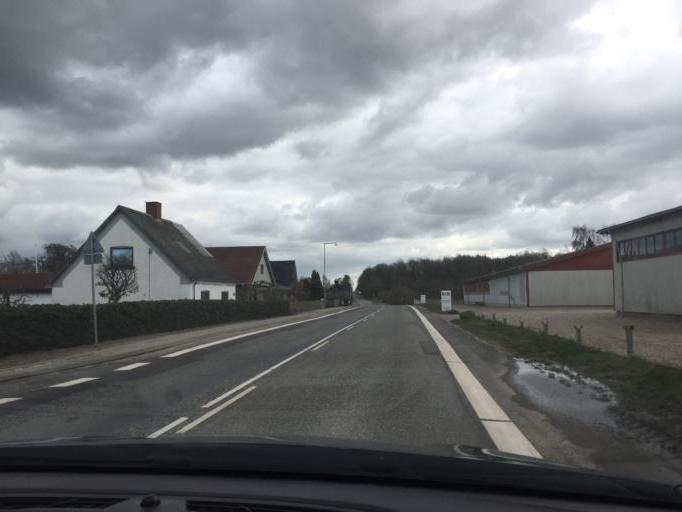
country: DK
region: South Denmark
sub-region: Kerteminde Kommune
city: Langeskov
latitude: 55.3068
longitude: 10.5880
